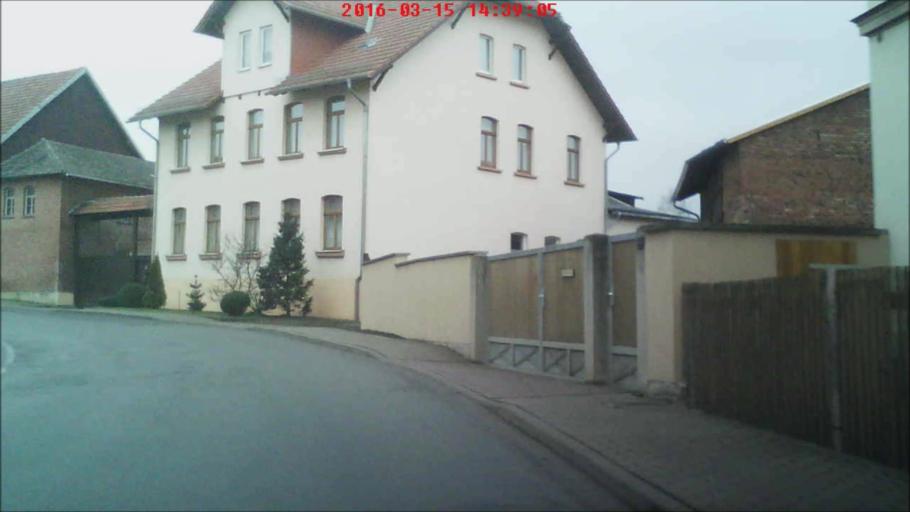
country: DE
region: Thuringia
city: Elxleben
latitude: 50.8689
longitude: 11.0537
